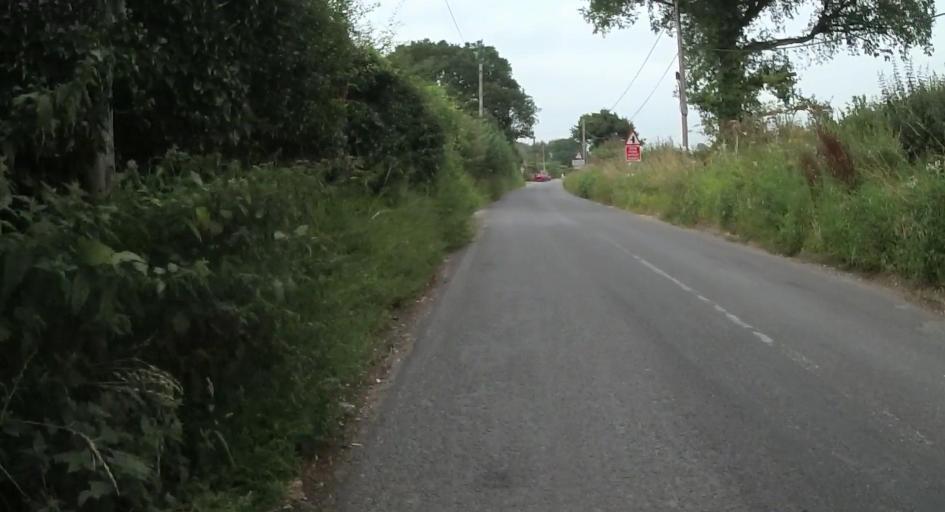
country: GB
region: England
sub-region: Hampshire
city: Old Basing
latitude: 51.2252
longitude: -1.0072
